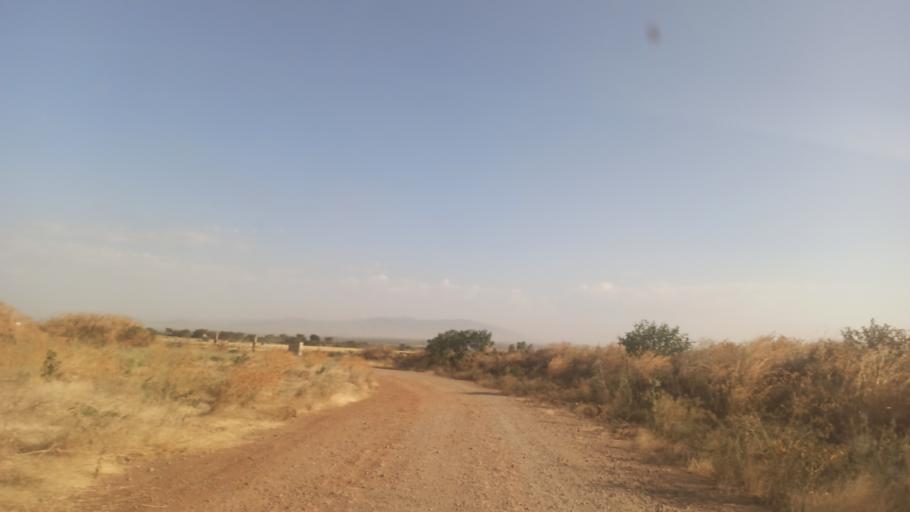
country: ET
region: Oromiya
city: Ziway
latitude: 7.9344
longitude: 38.6208
